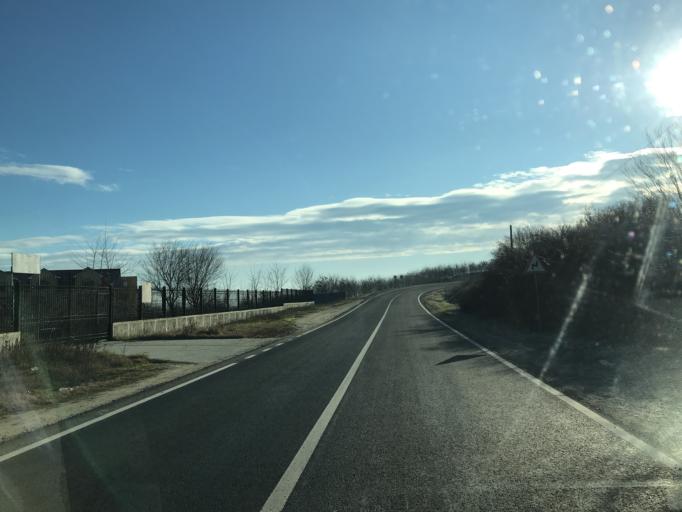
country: RO
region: Olt
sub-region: Comuna Ganeasa
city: Ganeasa
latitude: 44.3962
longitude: 24.2793
